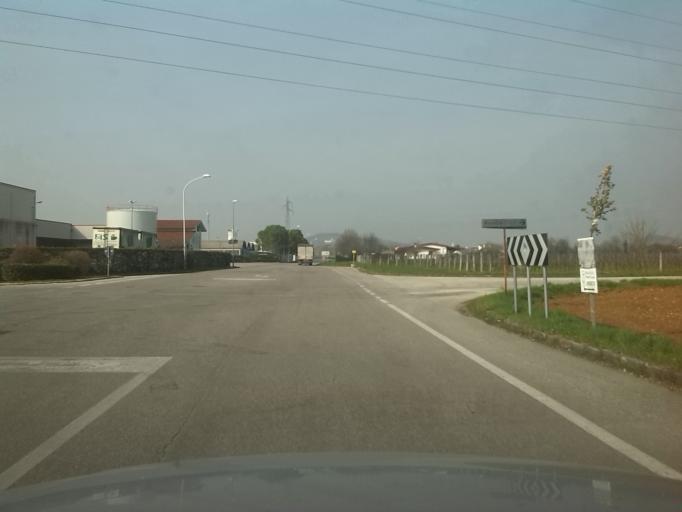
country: IT
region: Friuli Venezia Giulia
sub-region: Provincia di Udine
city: San Giovanni al Natisone
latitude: 45.9740
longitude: 13.4252
